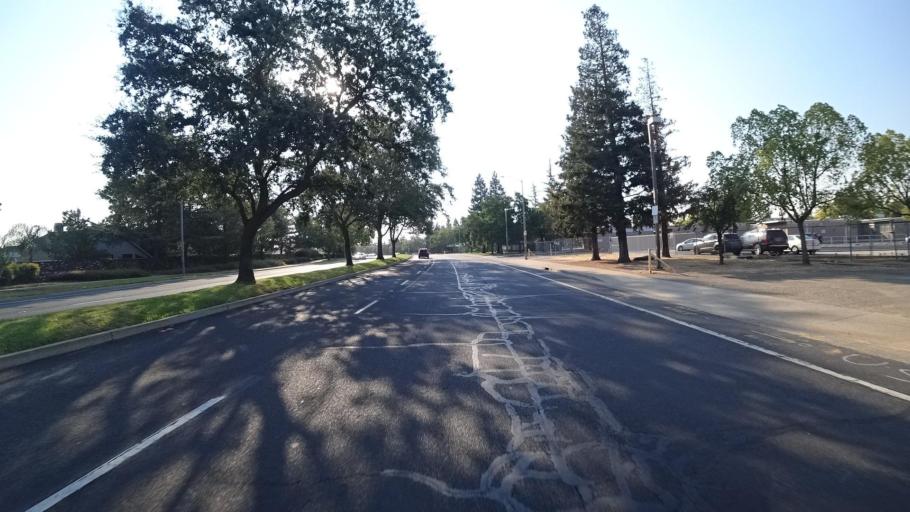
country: US
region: California
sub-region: Sacramento County
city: Laguna
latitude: 38.4308
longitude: -121.4284
